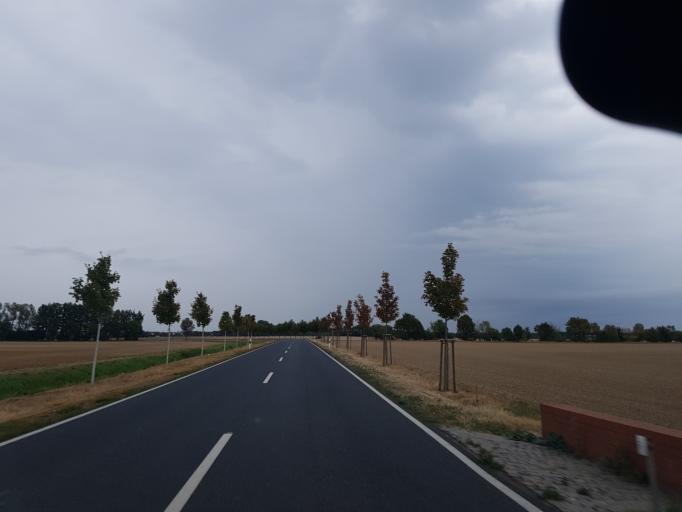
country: DE
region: Saxony-Anhalt
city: Jessen
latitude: 51.7590
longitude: 12.8957
